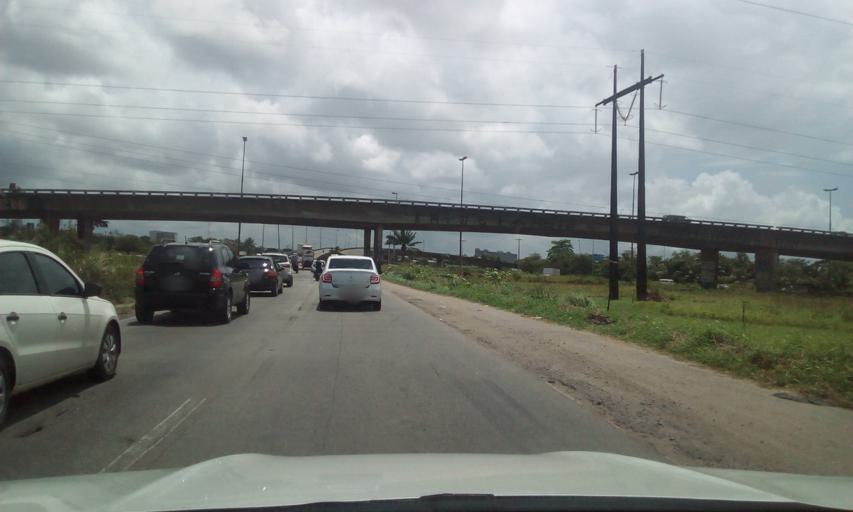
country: BR
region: Pernambuco
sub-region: Recife
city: Recife
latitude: -8.0681
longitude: -34.9426
